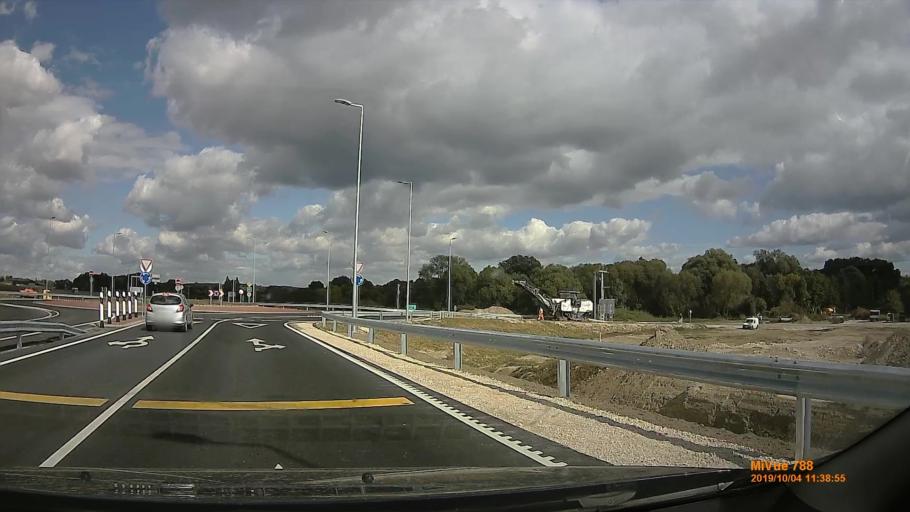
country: HU
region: Somogy
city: Karad
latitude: 46.5518
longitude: 17.8153
